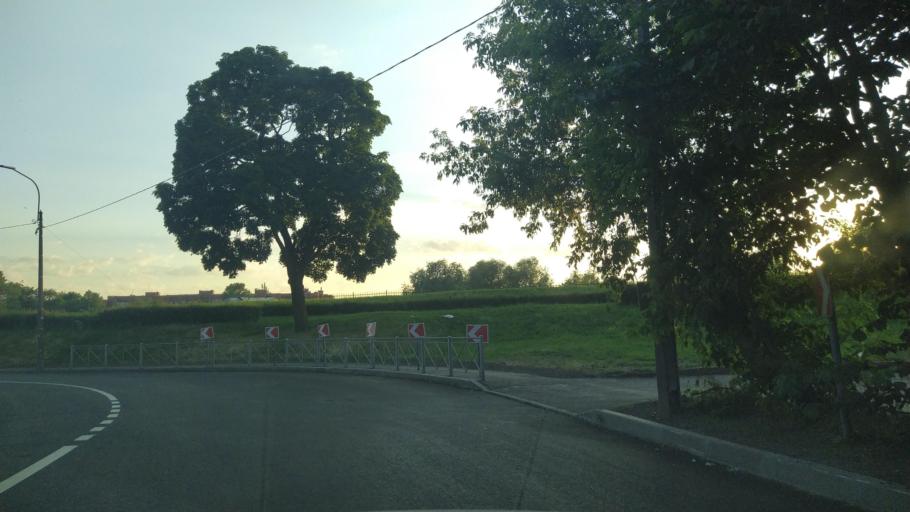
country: RU
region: St.-Petersburg
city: Kronshtadt
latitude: 60.0025
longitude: 29.7641
